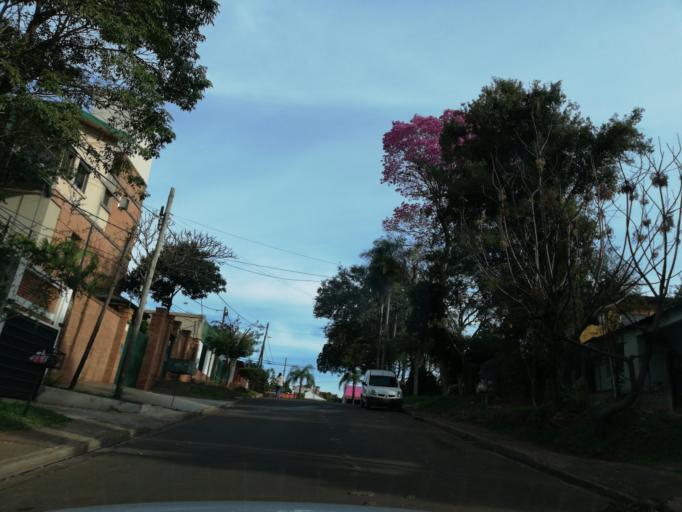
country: AR
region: Misiones
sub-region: Departamento de Capital
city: Posadas
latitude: -27.3583
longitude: -55.9140
